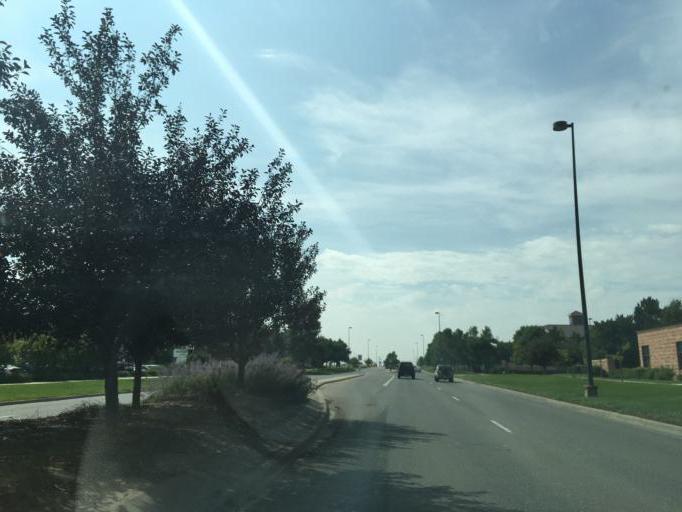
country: US
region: Colorado
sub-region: Adams County
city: Aurora
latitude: 39.8230
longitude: -104.7720
